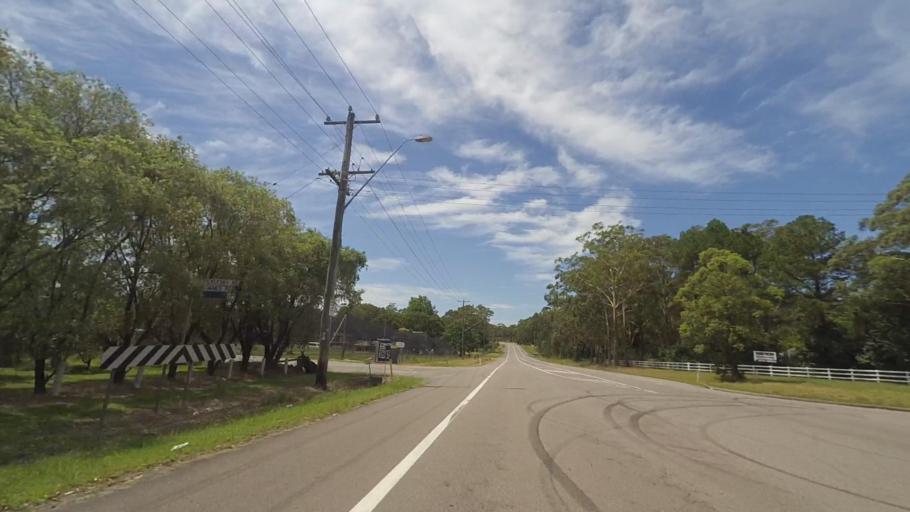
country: AU
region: New South Wales
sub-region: Port Stephens Shire
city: Medowie
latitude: -32.7530
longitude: 151.8682
